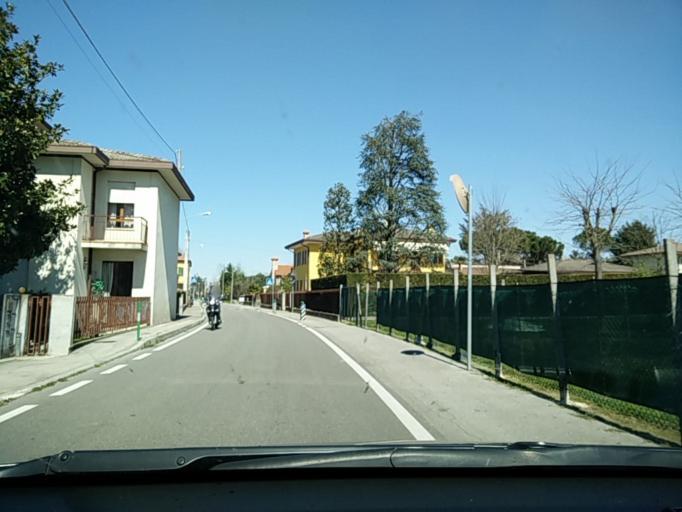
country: IT
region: Veneto
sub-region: Provincia di Padova
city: Sarmeola
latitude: 45.4192
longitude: 11.8387
